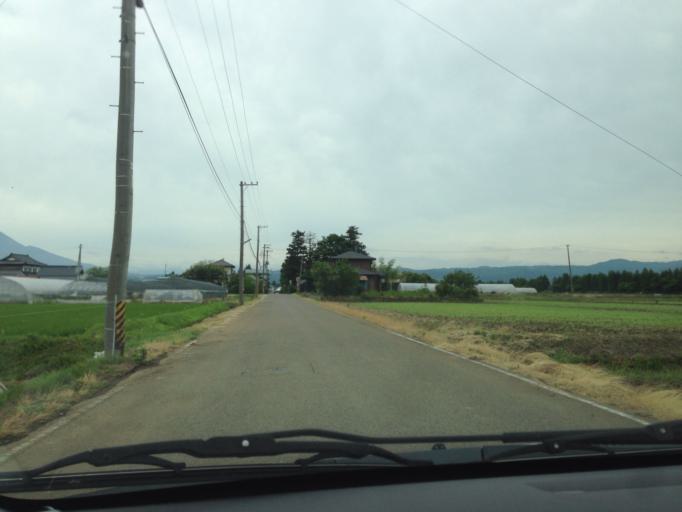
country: JP
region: Fukushima
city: Kitakata
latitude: 37.5369
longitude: 139.8909
